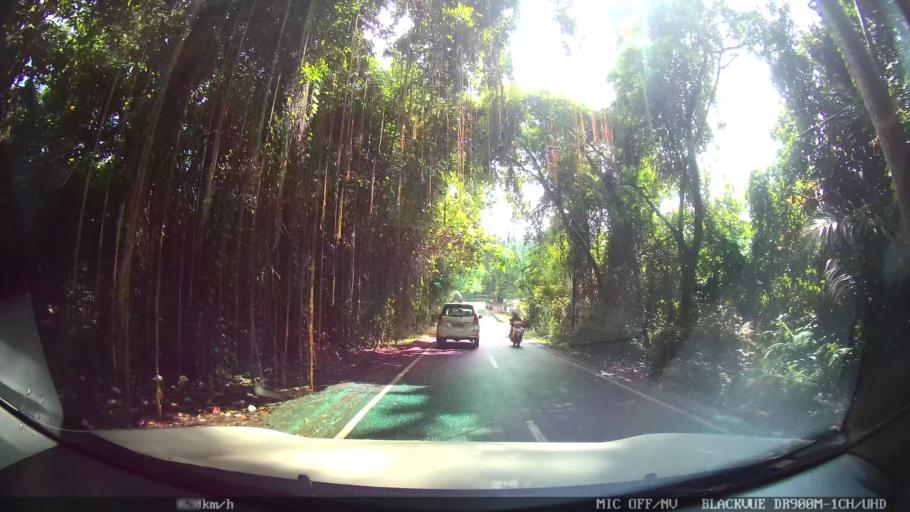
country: ID
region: Bali
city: Banjar Tebongkang
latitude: -8.5463
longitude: 115.2546
